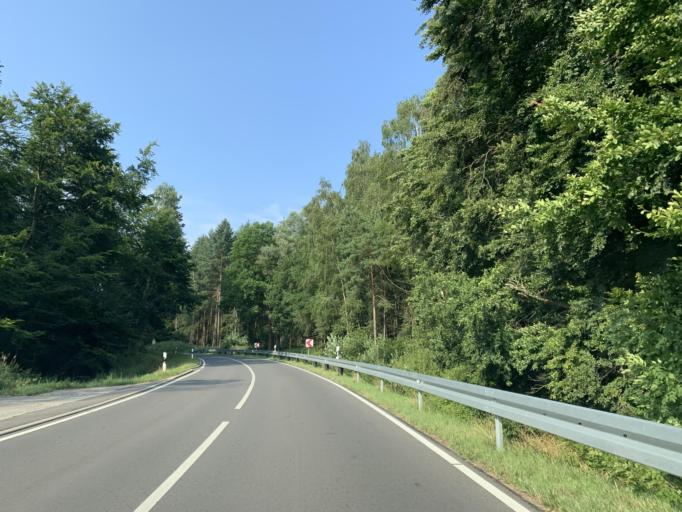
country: DE
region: Mecklenburg-Vorpommern
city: Wustrow
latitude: 53.4211
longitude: 13.1816
